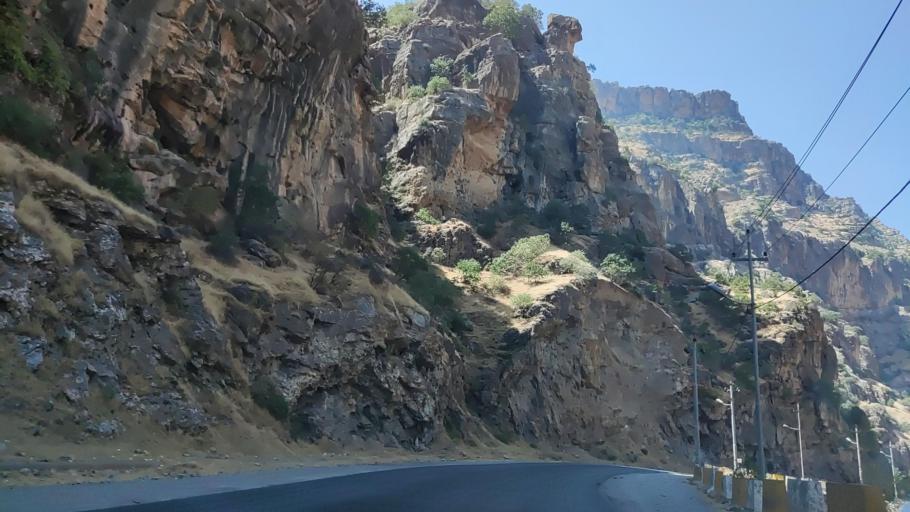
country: IQ
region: Arbil
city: Ruwandiz
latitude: 36.6322
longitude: 44.4898
